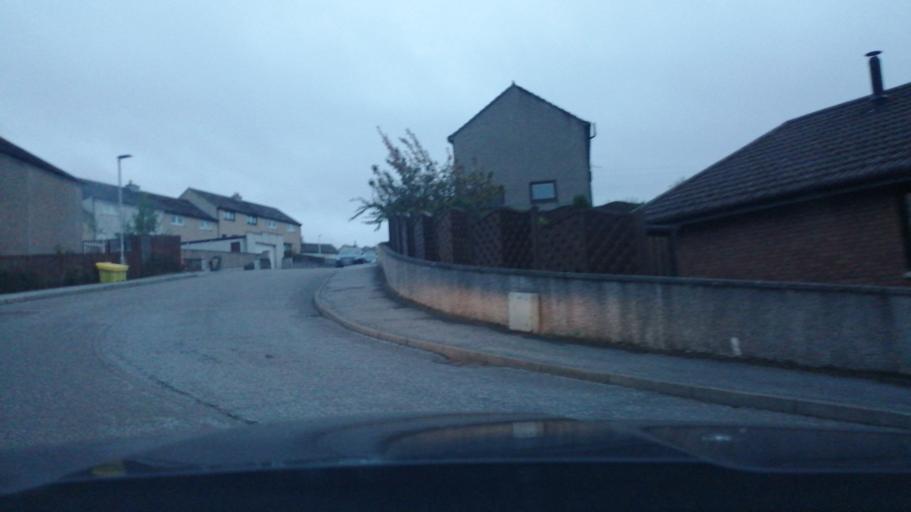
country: GB
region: Scotland
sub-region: Moray
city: Keith
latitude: 57.5417
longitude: -2.9561
